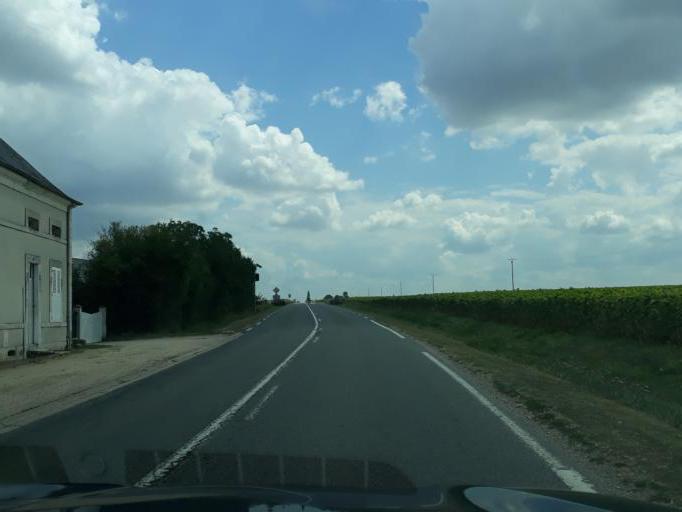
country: FR
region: Centre
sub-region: Departement du Cher
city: Avord
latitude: 47.0418
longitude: 2.5684
